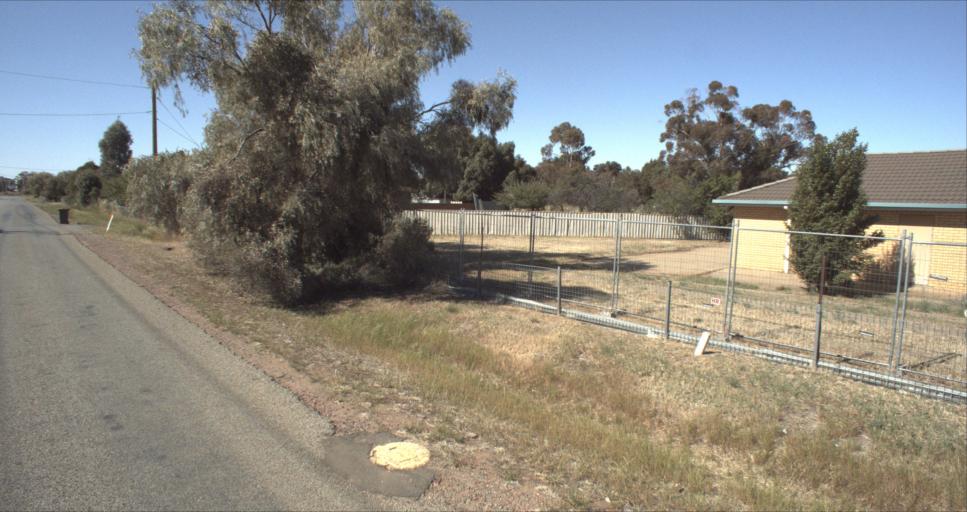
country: AU
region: New South Wales
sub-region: Leeton
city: Leeton
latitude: -34.5556
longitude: 146.3845
